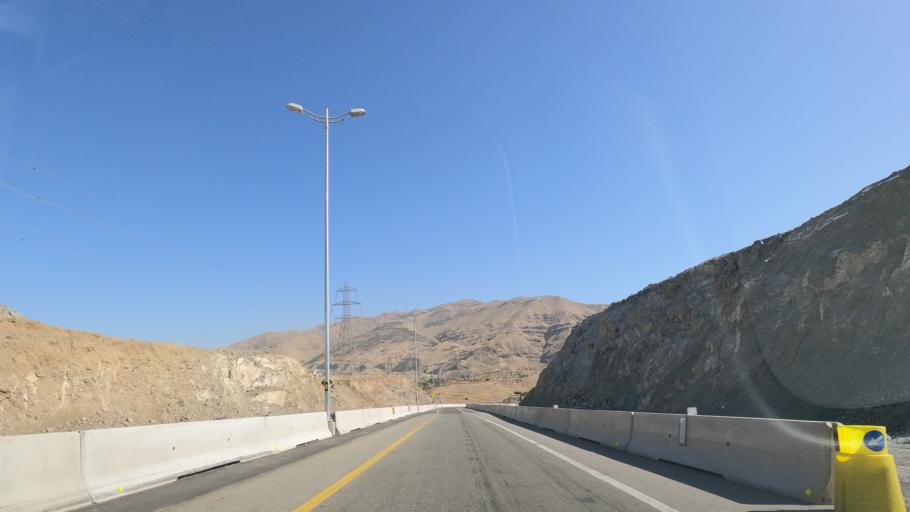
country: IR
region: Alborz
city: Karaj
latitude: 35.8202
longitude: 51.0377
